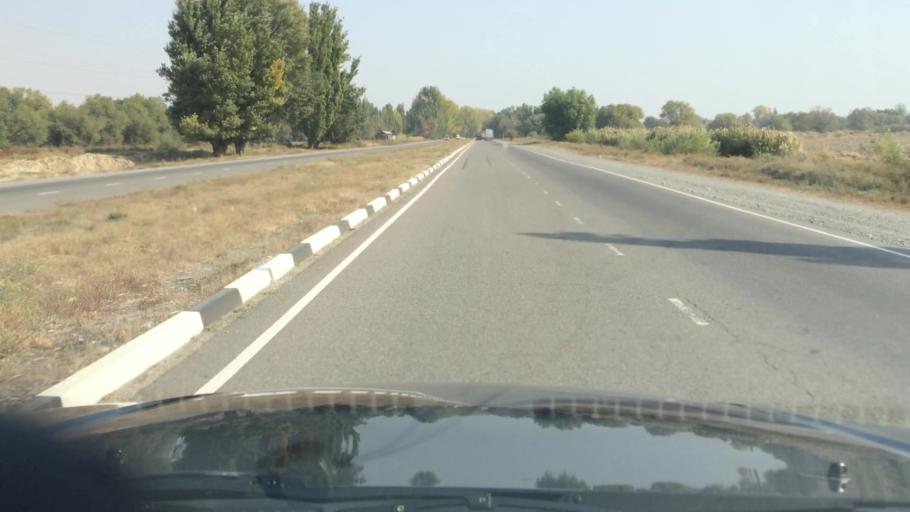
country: KG
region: Chuy
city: Kant
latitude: 42.9705
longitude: 74.8509
